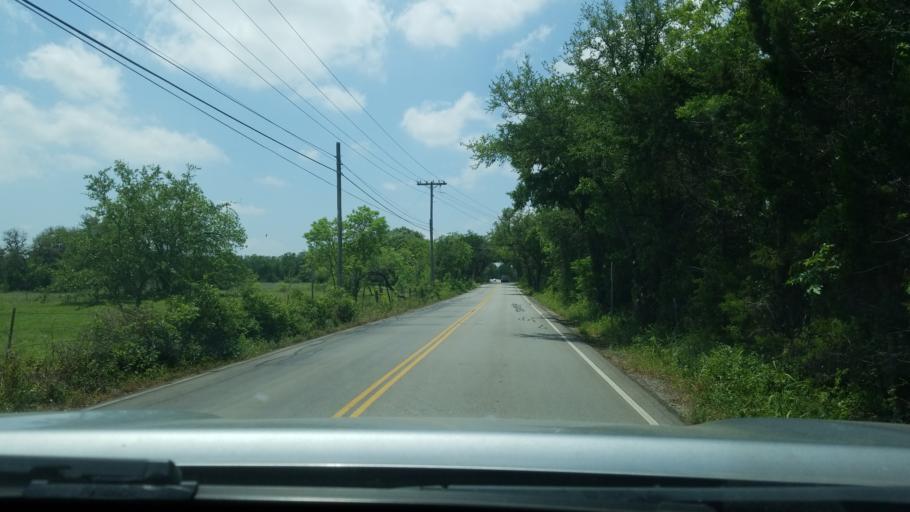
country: US
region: Texas
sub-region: Hays County
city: Woodcreek
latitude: 30.0298
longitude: -98.1234
